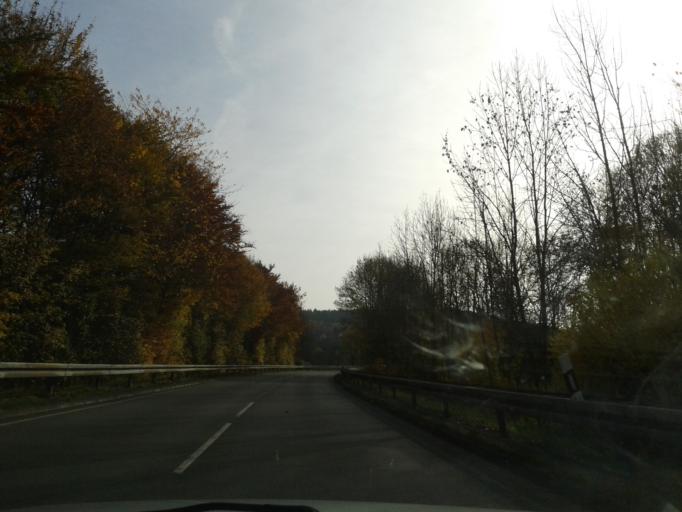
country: DE
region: North Rhine-Westphalia
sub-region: Regierungsbezirk Arnsberg
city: Ruthen
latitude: 51.4369
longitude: 8.4465
